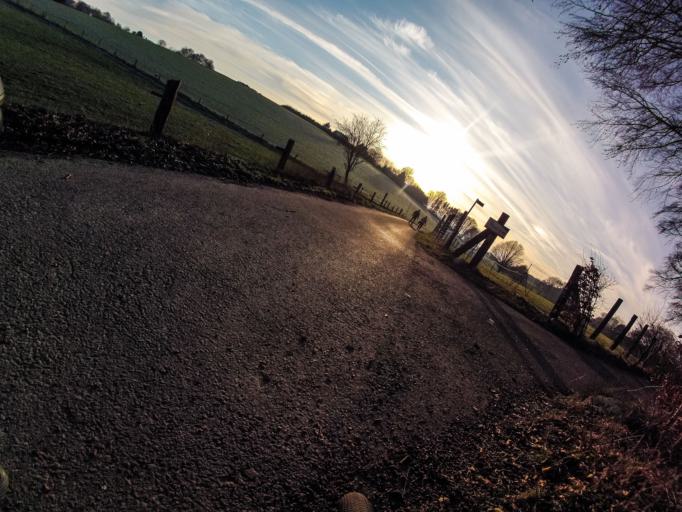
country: DE
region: North Rhine-Westphalia
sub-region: Regierungsbezirk Munster
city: Mettingen
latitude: 52.2783
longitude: 7.8067
